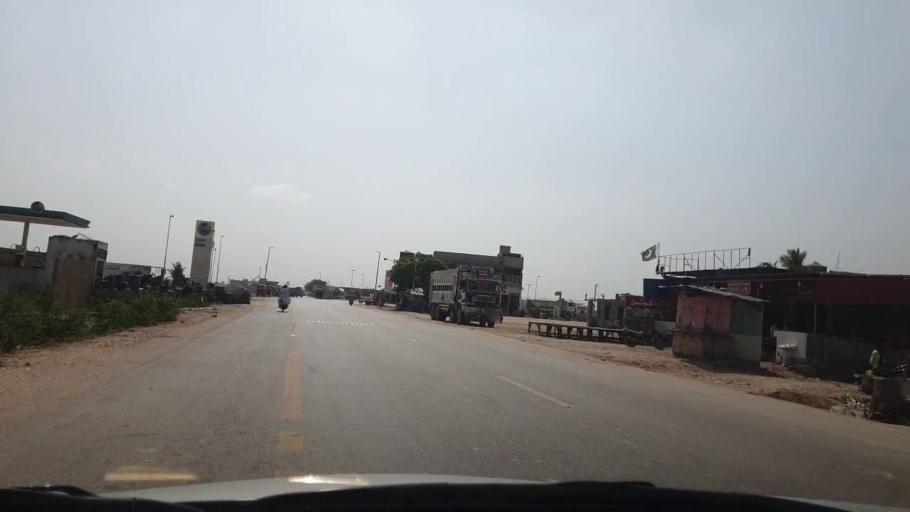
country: PK
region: Sindh
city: Matli
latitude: 25.0605
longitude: 68.6363
